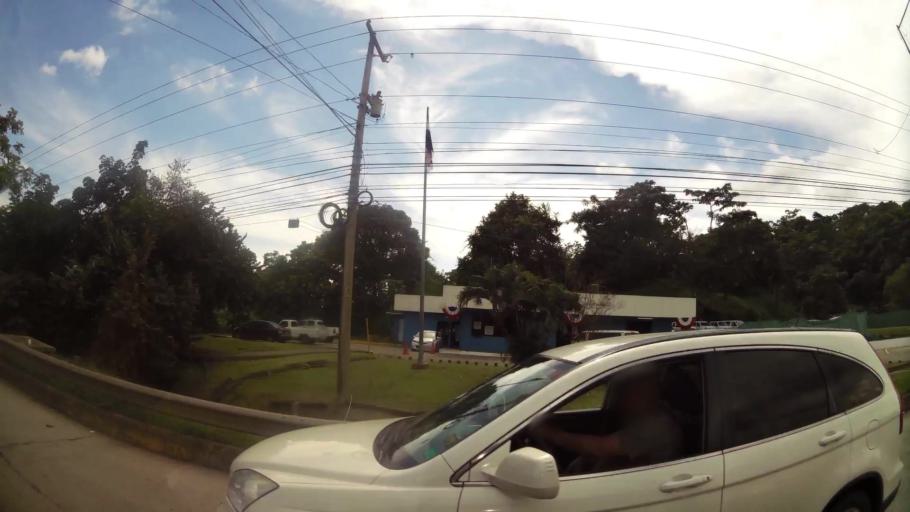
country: PA
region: Panama
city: Panama
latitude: 9.0335
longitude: -79.5368
